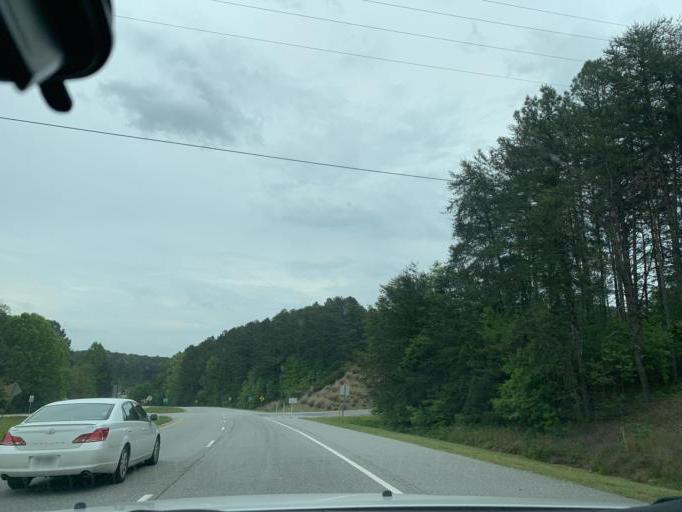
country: US
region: Georgia
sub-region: Forsyth County
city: Cumming
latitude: 34.2093
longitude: -84.1208
